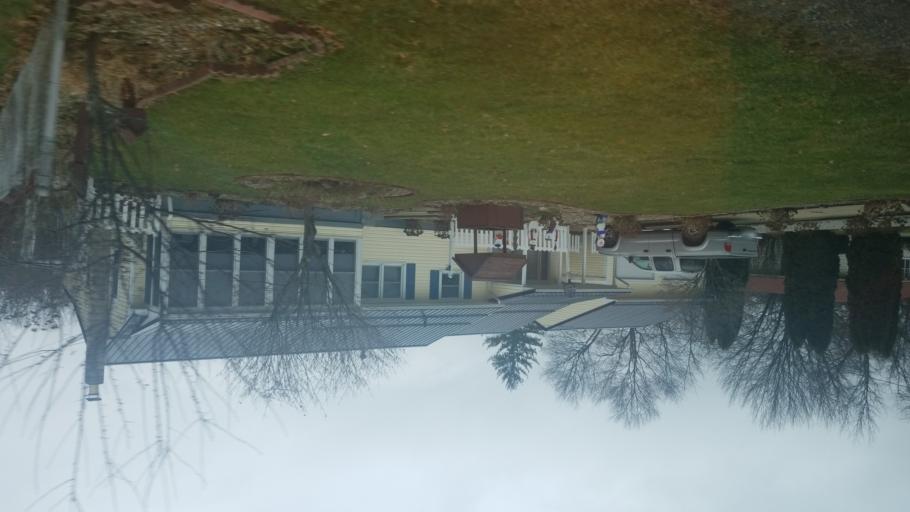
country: US
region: Ohio
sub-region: Crawford County
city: Galion
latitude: 40.7231
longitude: -82.7991
